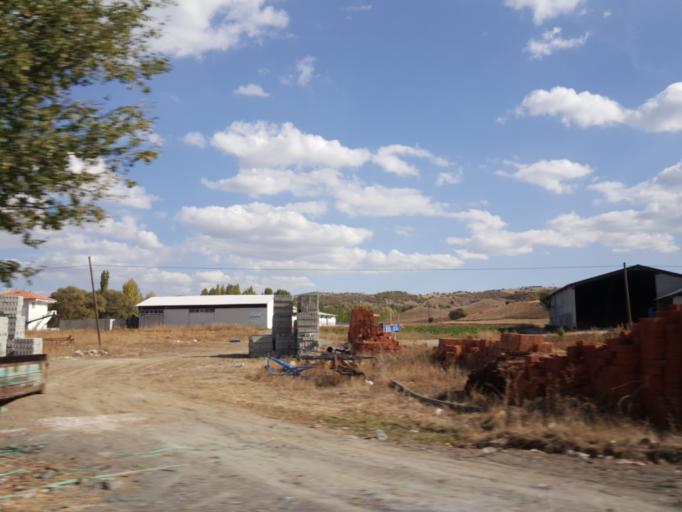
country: TR
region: Tokat
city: Sulusaray
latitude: 39.9789
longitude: 36.0594
